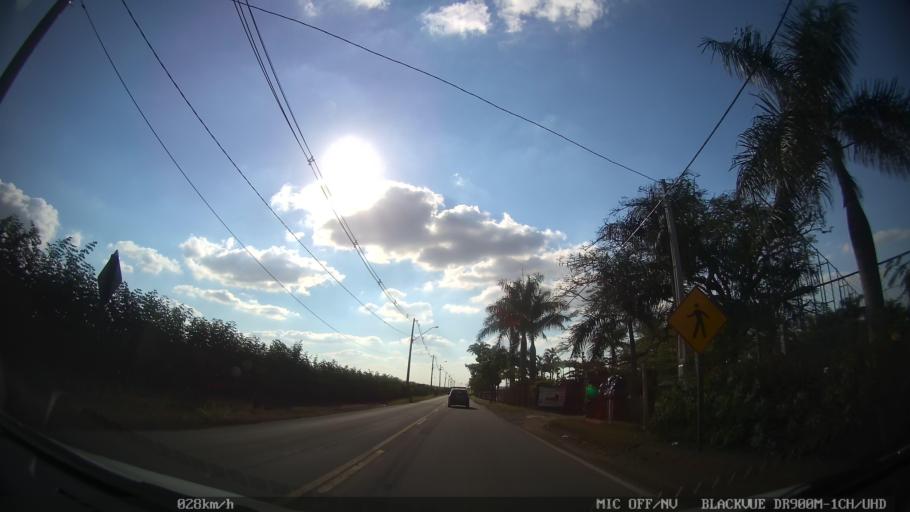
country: BR
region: Sao Paulo
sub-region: Nova Odessa
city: Nova Odessa
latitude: -22.8085
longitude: -47.3318
